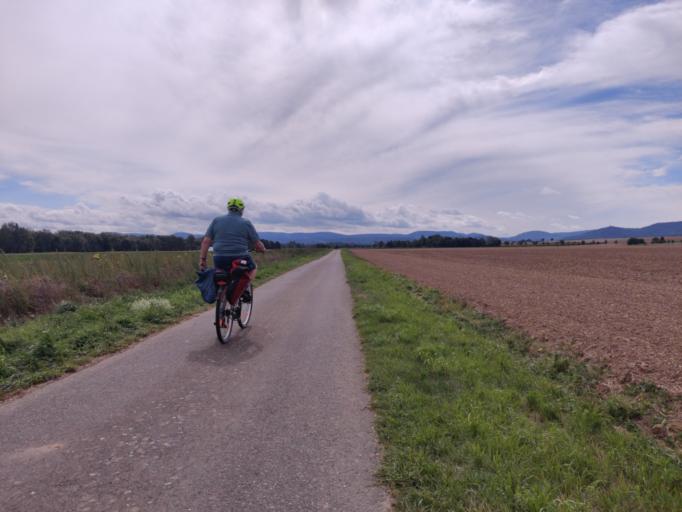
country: DE
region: Lower Saxony
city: Liebenburg
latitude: 51.9966
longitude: 10.3708
